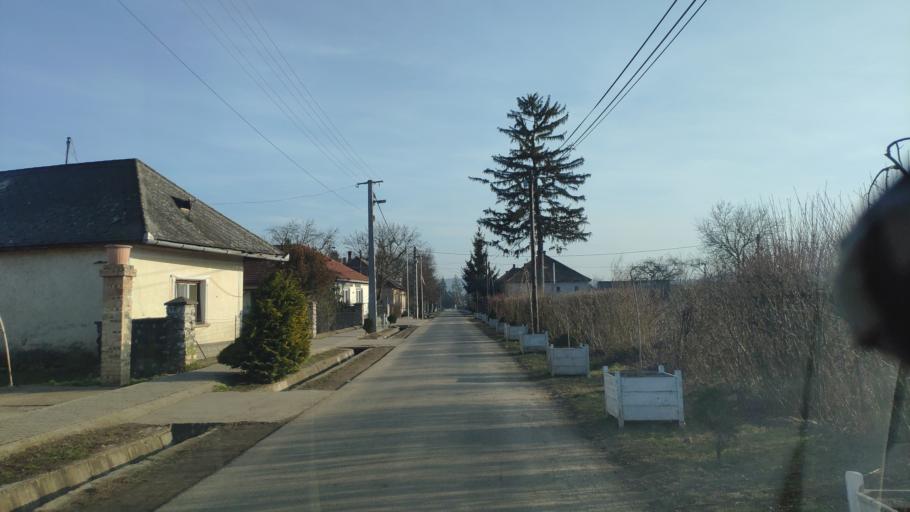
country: HU
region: Borsod-Abauj-Zemplen
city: Szendro
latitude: 48.5605
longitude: 20.7863
